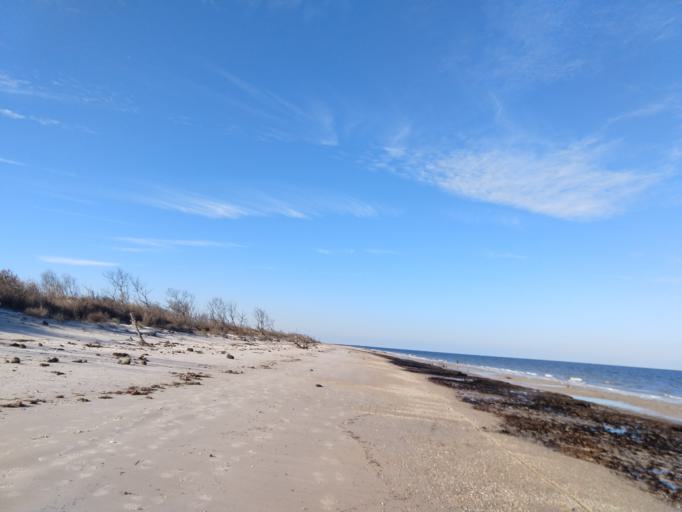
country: US
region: Virginia
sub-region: City of Poquoson
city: Poquoson
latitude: 37.0951
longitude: -76.2752
